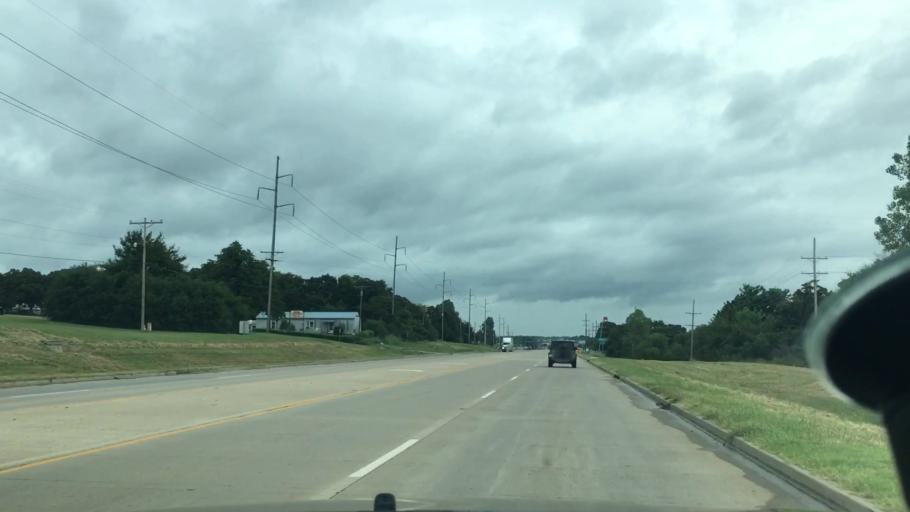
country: US
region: Oklahoma
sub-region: Seminole County
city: Seminole
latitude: 35.2531
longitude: -96.6712
